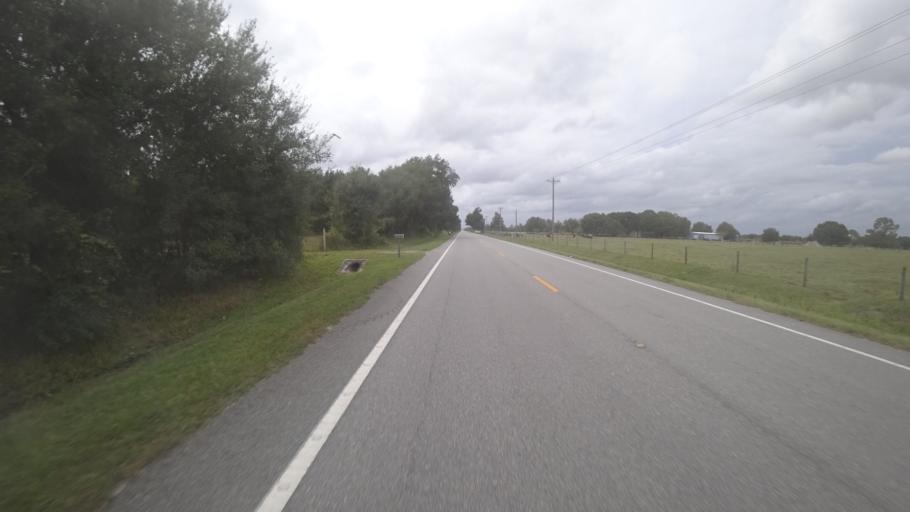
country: US
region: Florida
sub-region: Hardee County
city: Wauchula
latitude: 27.4599
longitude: -82.1128
